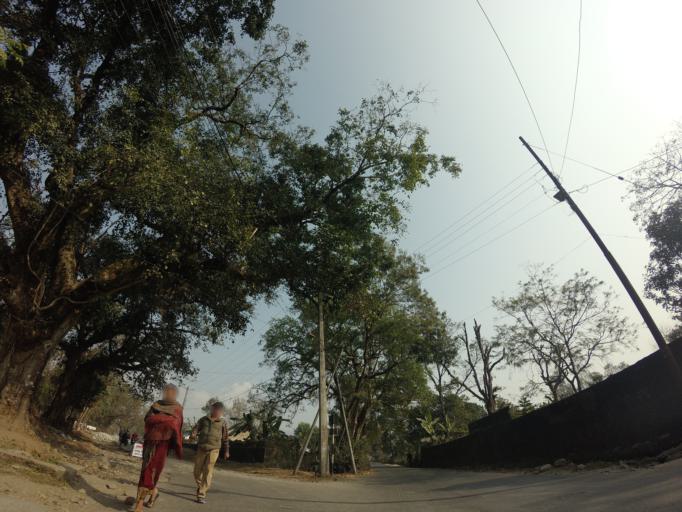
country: NP
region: Western Region
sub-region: Gandaki Zone
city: Pokhara
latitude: 28.2024
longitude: 83.9711
